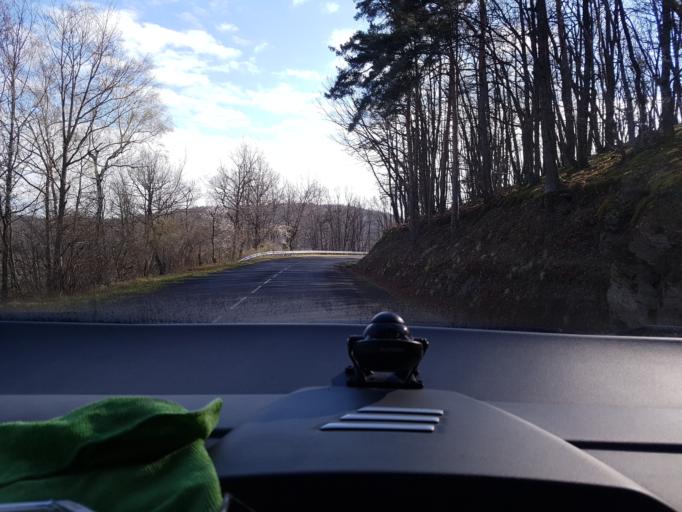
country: FR
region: Auvergne
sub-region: Departement du Cantal
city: Massiac
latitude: 45.2369
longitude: 3.2022
